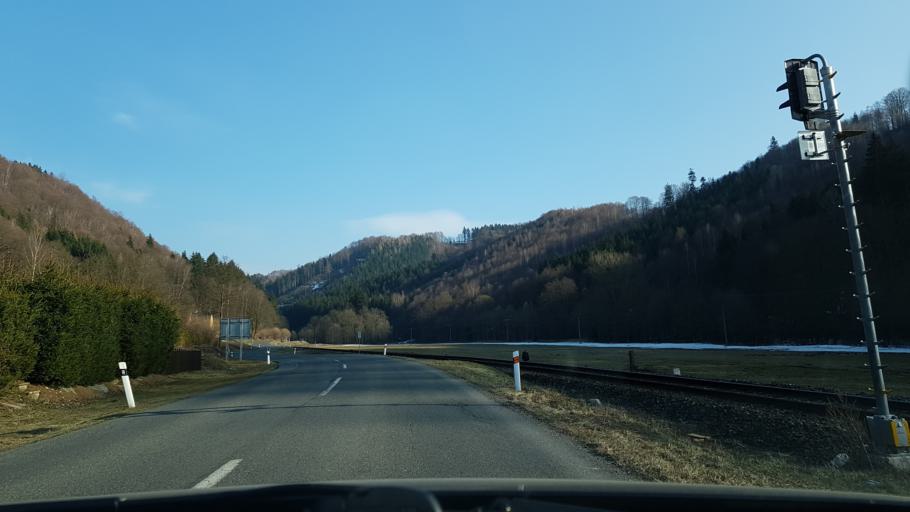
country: CZ
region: Olomoucky
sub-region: Okres Sumperk
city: Hanusovice
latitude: 50.0795
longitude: 16.9437
